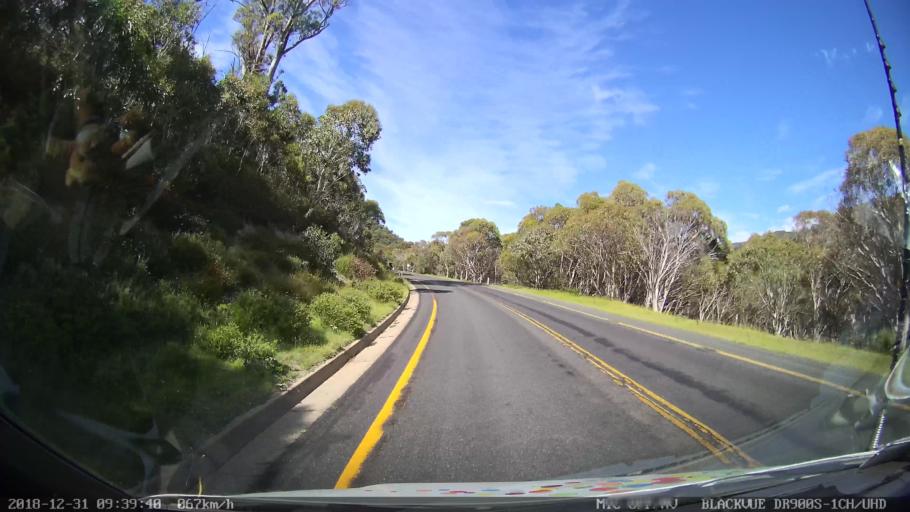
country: AU
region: New South Wales
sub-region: Snowy River
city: Jindabyne
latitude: -36.4797
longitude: 148.3520
